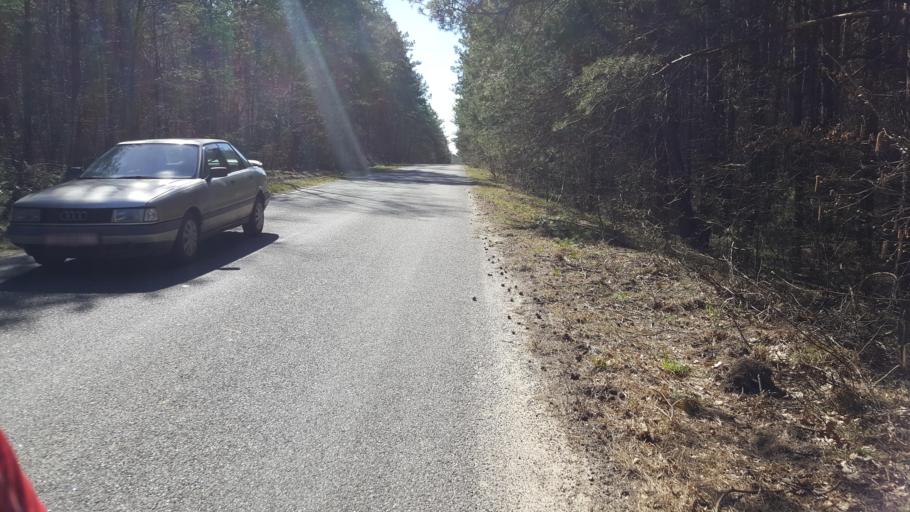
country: BY
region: Brest
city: Kamyanyets
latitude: 52.2963
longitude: 23.8235
